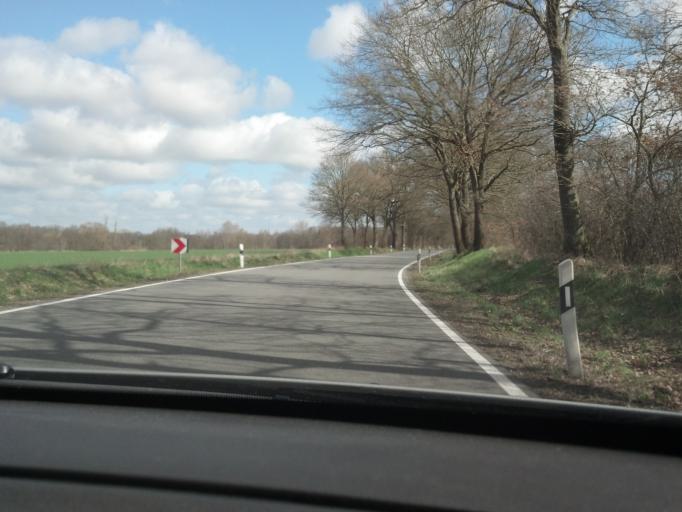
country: DE
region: Schleswig-Holstein
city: Langenlehsten
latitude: 53.4545
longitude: 10.7724
